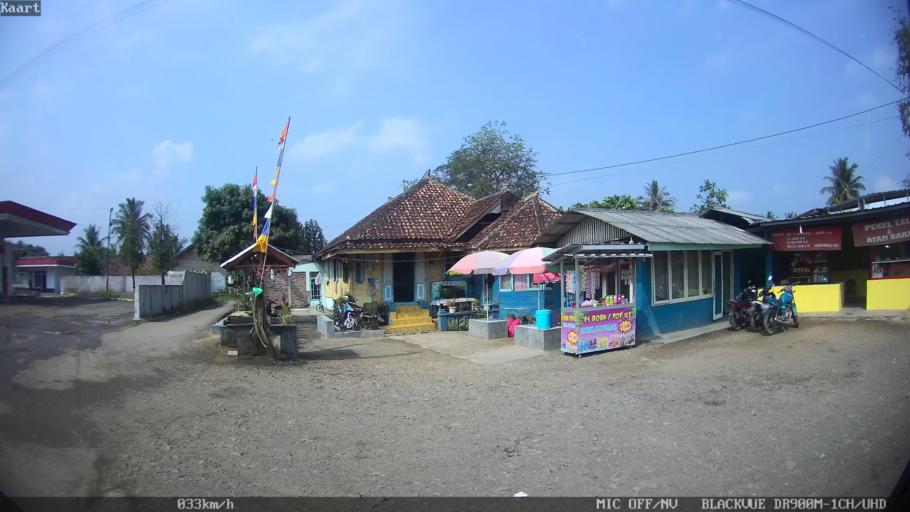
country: ID
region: Lampung
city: Gedongtataan
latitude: -5.3793
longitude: 105.0943
